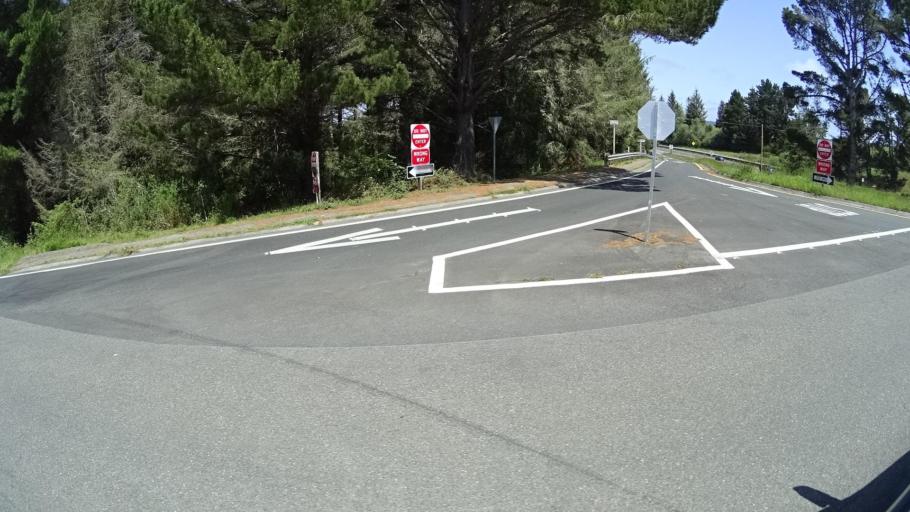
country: US
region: California
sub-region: Humboldt County
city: Fortuna
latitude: 40.6419
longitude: -124.2102
